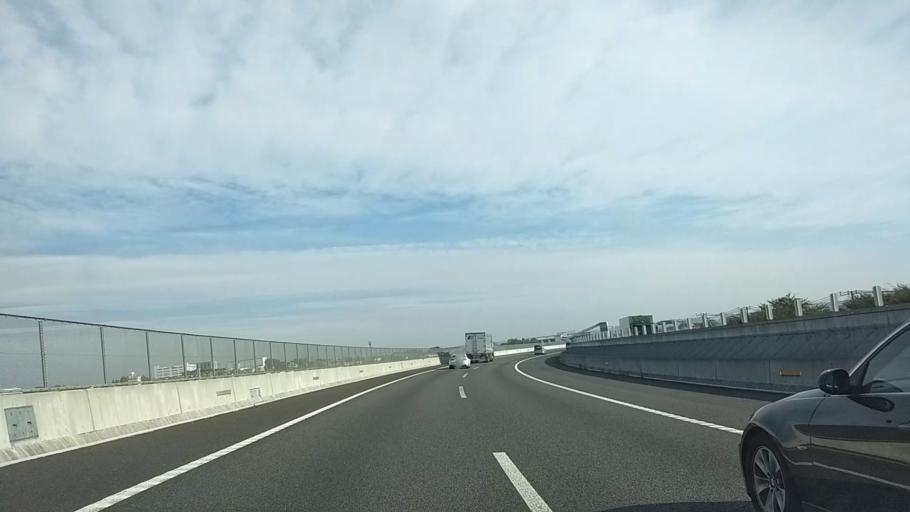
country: JP
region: Kanagawa
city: Atsugi
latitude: 35.4576
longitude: 139.3721
